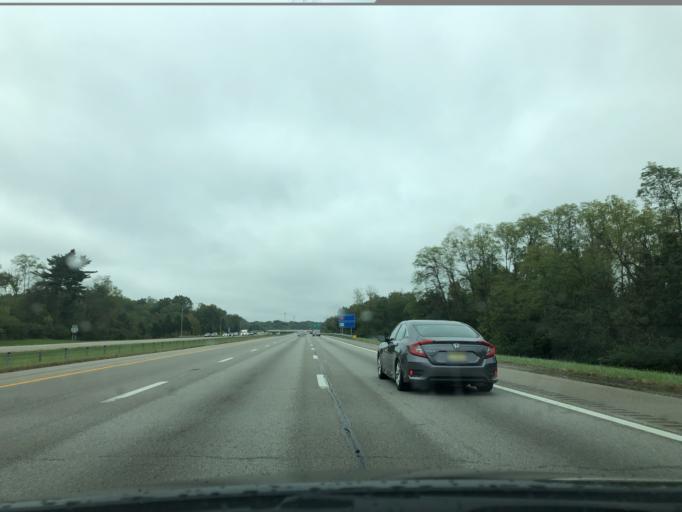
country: US
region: Ohio
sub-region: Hamilton County
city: The Village of Indian Hill
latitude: 39.2308
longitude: -84.2879
